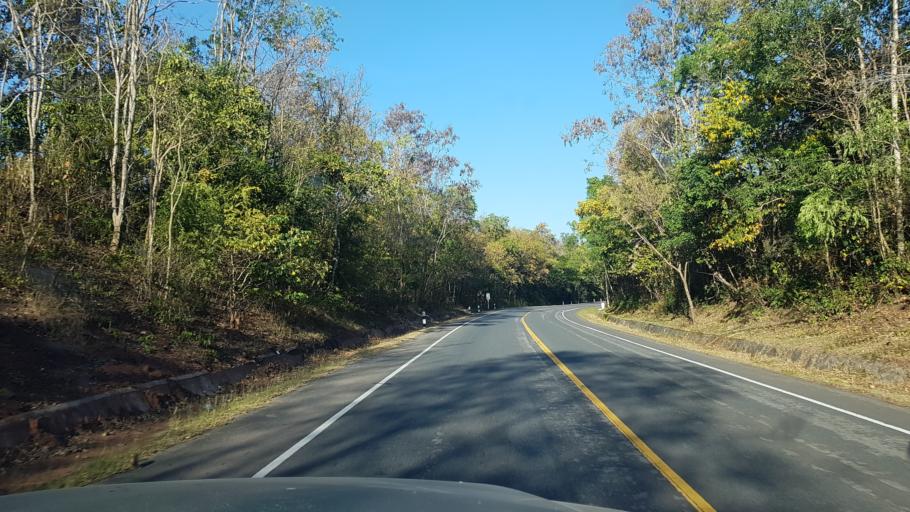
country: TH
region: Phetchabun
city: Lom Sak
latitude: 16.7504
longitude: 101.4537
